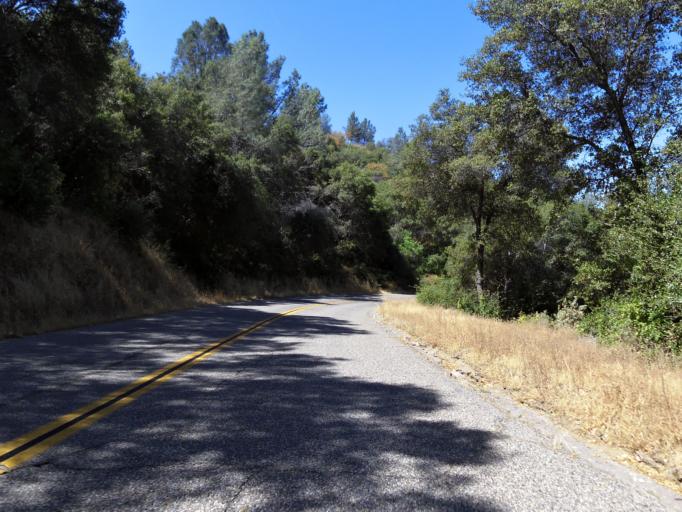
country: US
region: California
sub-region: Fresno County
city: Auberry
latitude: 37.1796
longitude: -119.5110
